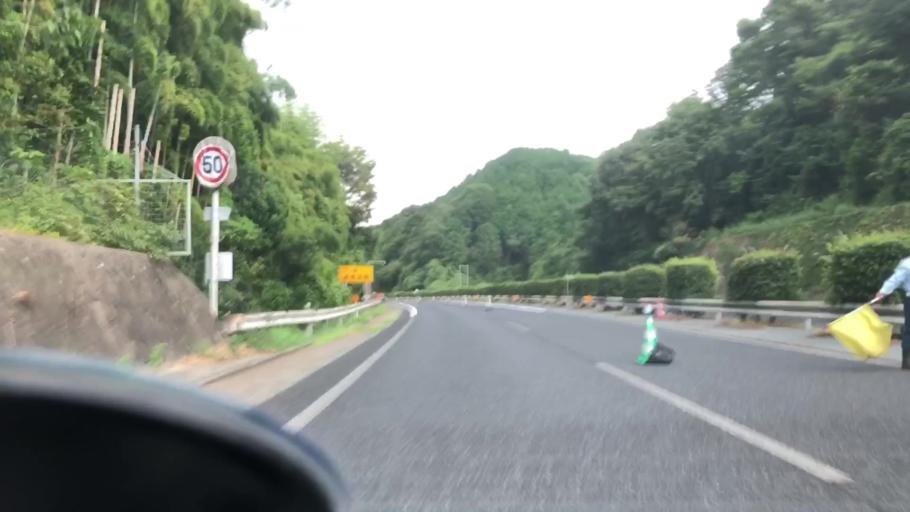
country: JP
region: Hyogo
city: Himeji
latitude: 34.9534
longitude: 134.7279
